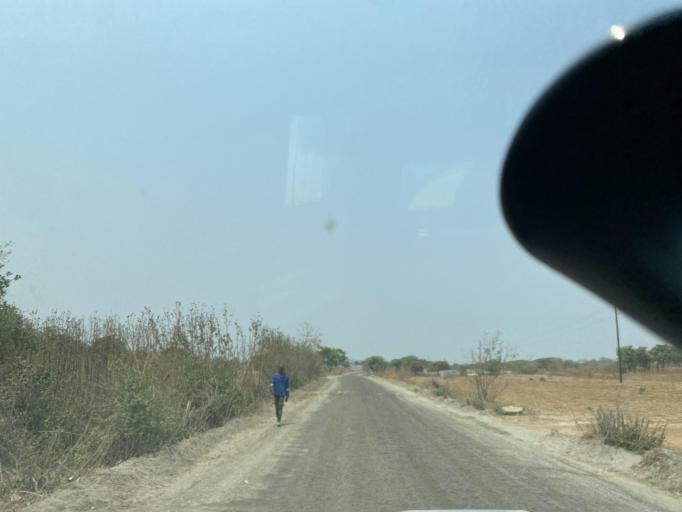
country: ZM
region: Lusaka
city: Lusaka
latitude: -15.5612
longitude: 28.4213
